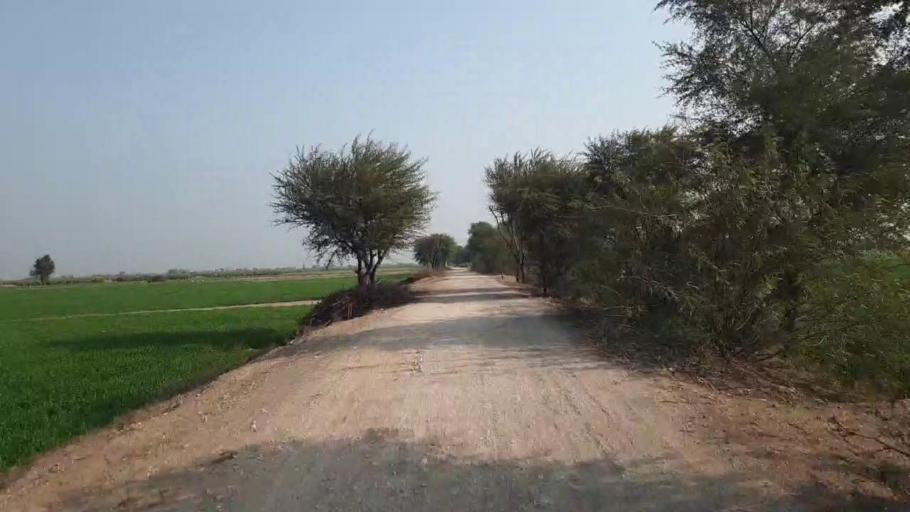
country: PK
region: Sindh
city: Hala
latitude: 25.8883
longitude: 68.4433
